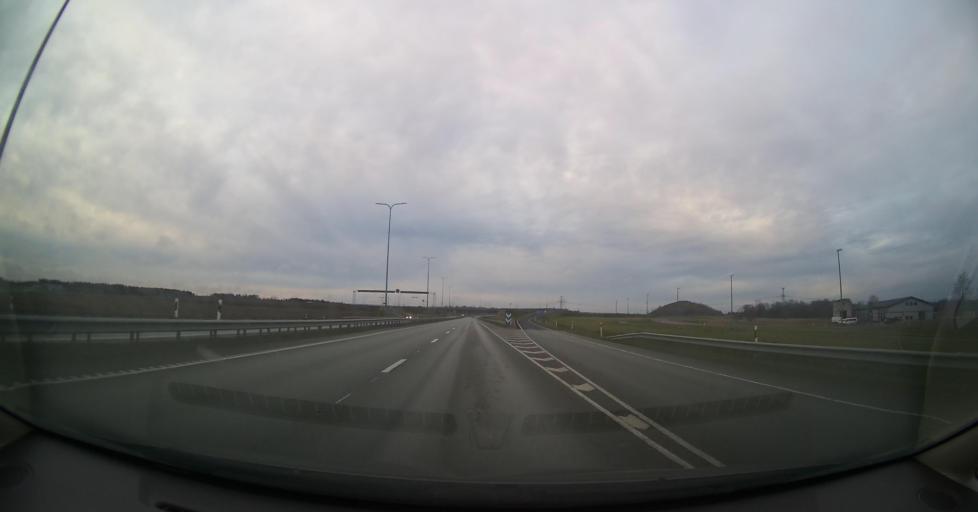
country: EE
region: Ida-Virumaa
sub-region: Johvi vald
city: Johvi
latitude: 59.3825
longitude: 27.3555
